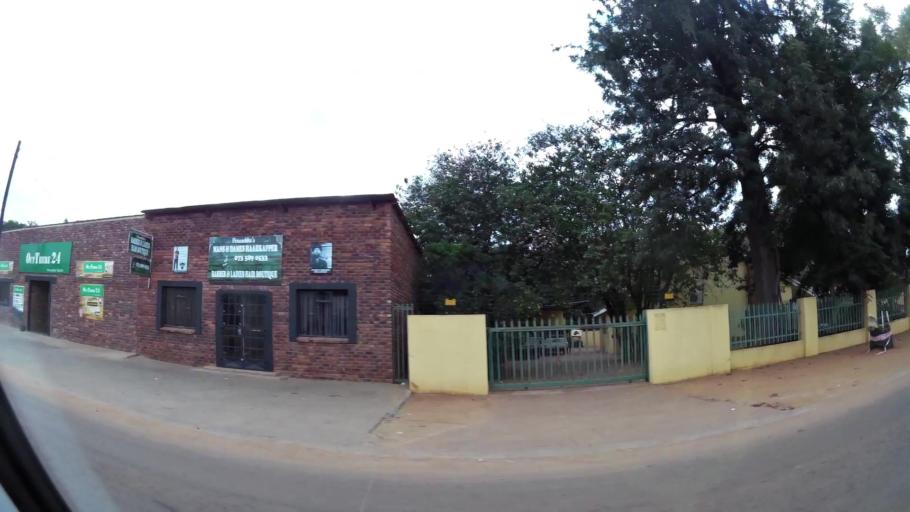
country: ZA
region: Limpopo
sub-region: Waterberg District Municipality
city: Modimolle
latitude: -24.5207
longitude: 28.7110
